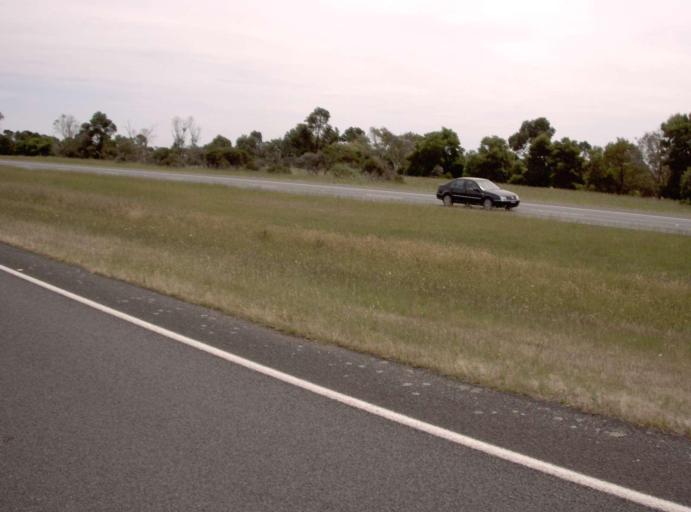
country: AU
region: Victoria
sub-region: Mornington Peninsula
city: Safety Beach
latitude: -38.3250
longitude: 144.9994
